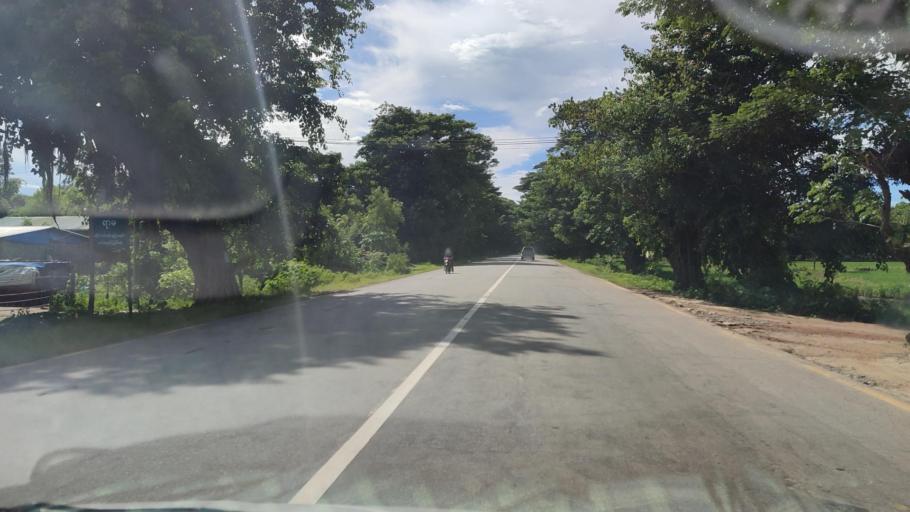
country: MM
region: Bago
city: Pyu
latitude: 18.2400
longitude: 96.5456
